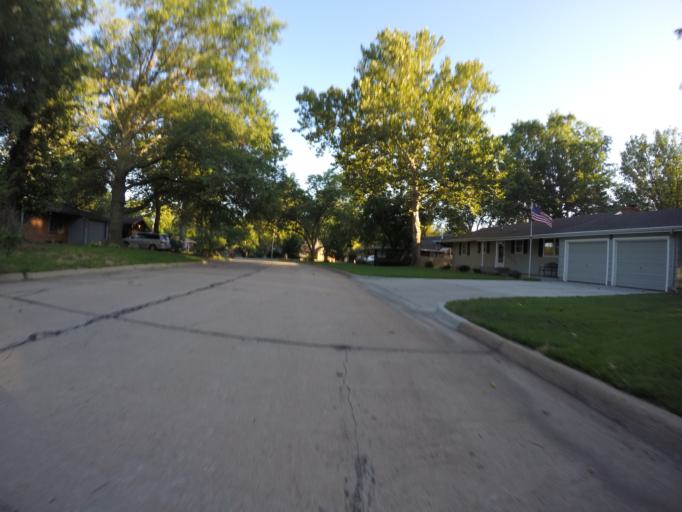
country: US
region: Kansas
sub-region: Riley County
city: Manhattan
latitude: 39.2030
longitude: -96.6103
